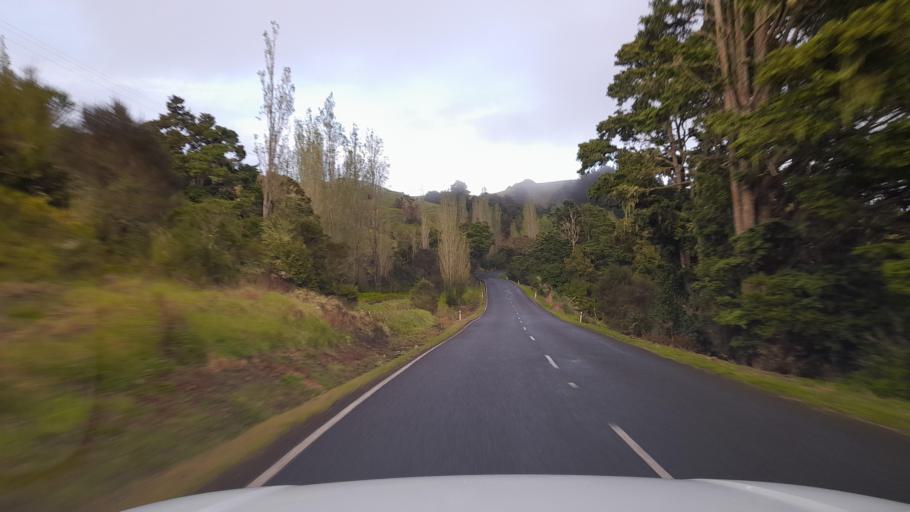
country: NZ
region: Northland
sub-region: Kaipara District
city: Dargaville
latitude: -35.7075
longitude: 173.9309
